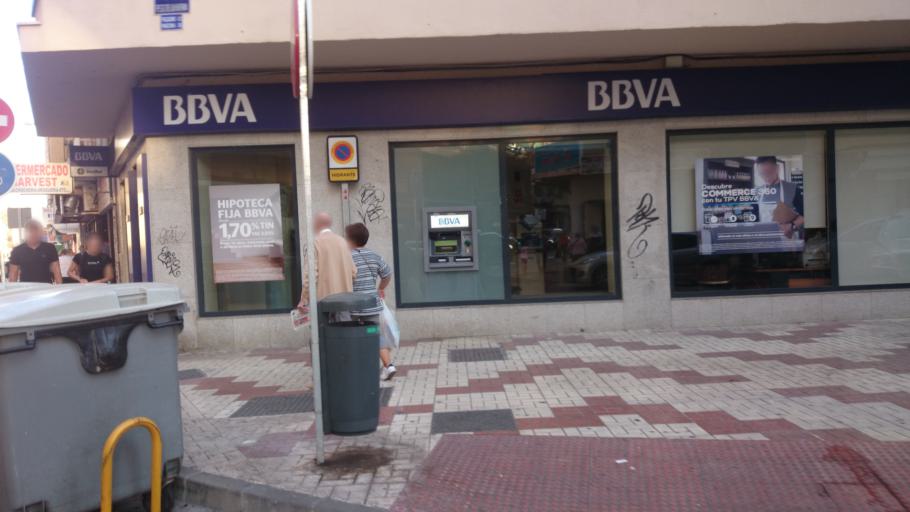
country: ES
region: Andalusia
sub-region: Provincia de Malaga
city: Malaga
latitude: 36.7216
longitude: -4.4310
